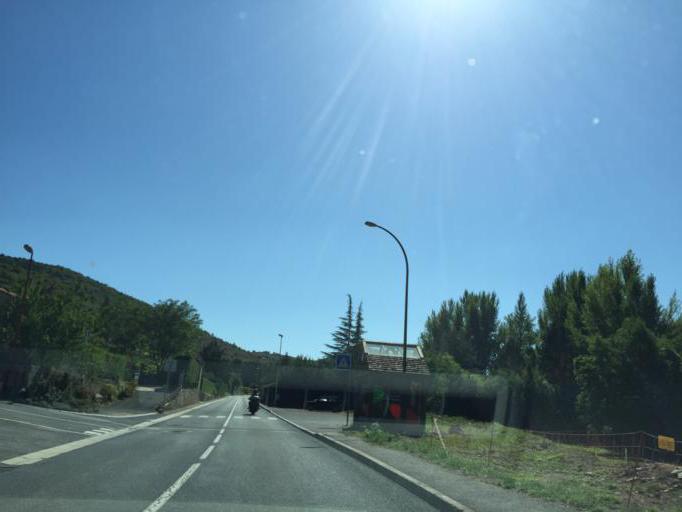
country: FR
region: Midi-Pyrenees
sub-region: Departement de l'Aveyron
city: Saint-Georges-de-Luzencon
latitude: 44.0429
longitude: 2.9056
